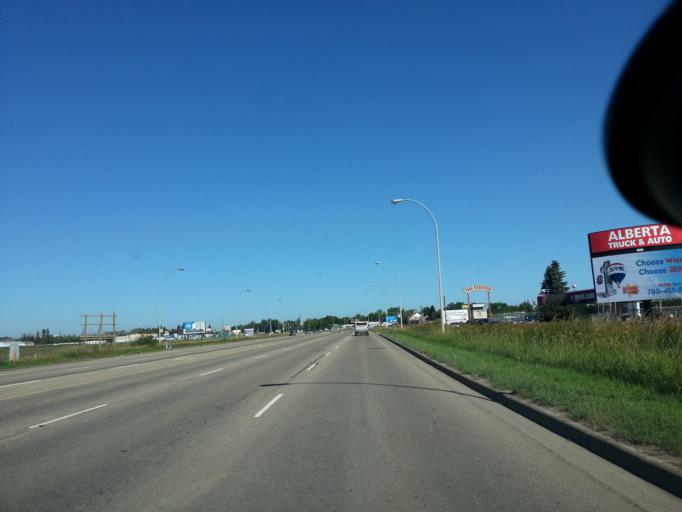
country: CA
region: Alberta
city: St. Albert
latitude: 53.6032
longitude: -113.5782
